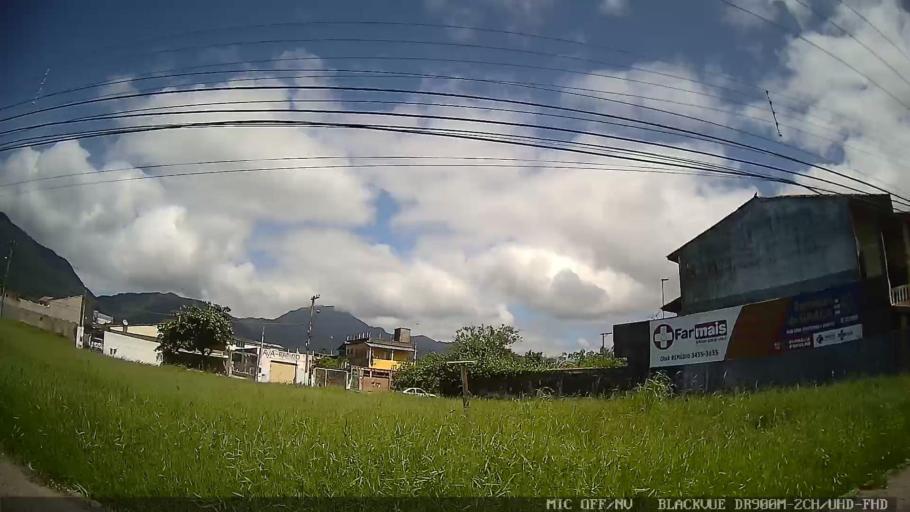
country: BR
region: Sao Paulo
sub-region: Peruibe
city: Peruibe
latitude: -24.3144
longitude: -47.0096
